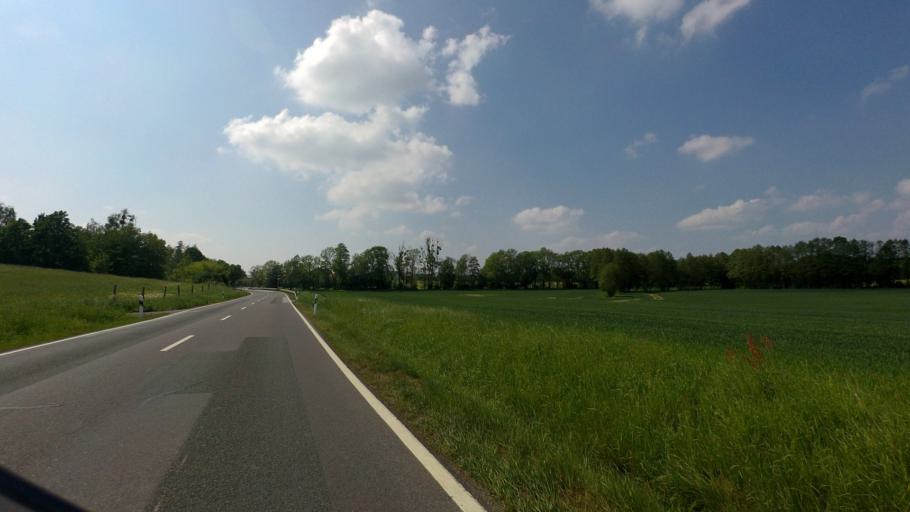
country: DE
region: Saxony
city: Weissenberg
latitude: 51.1878
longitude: 14.6286
